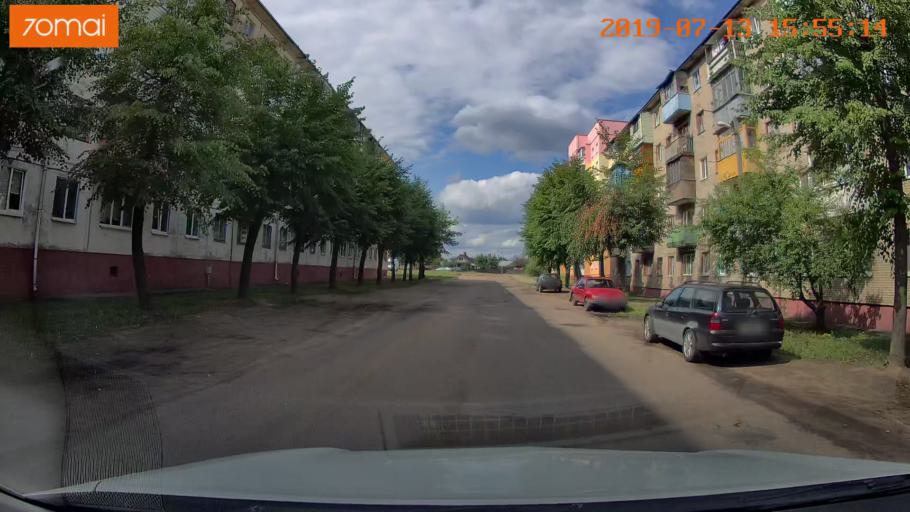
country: BY
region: Mogilev
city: Babruysk
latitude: 53.1407
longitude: 29.1988
